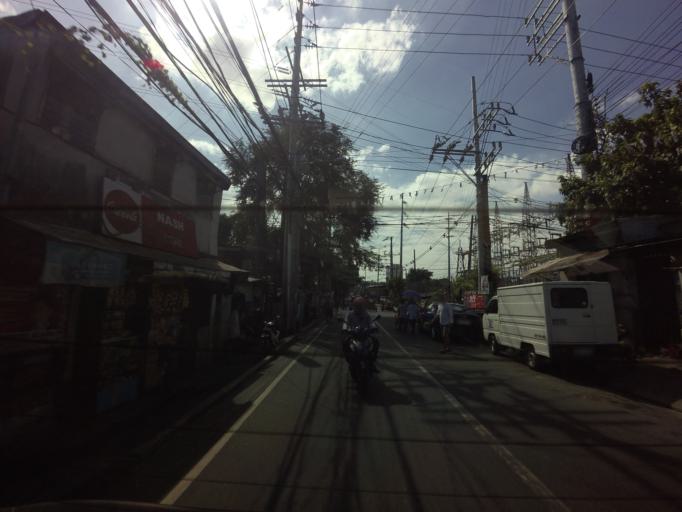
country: PH
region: Metro Manila
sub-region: San Juan
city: San Juan
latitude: 14.6142
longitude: 121.0133
